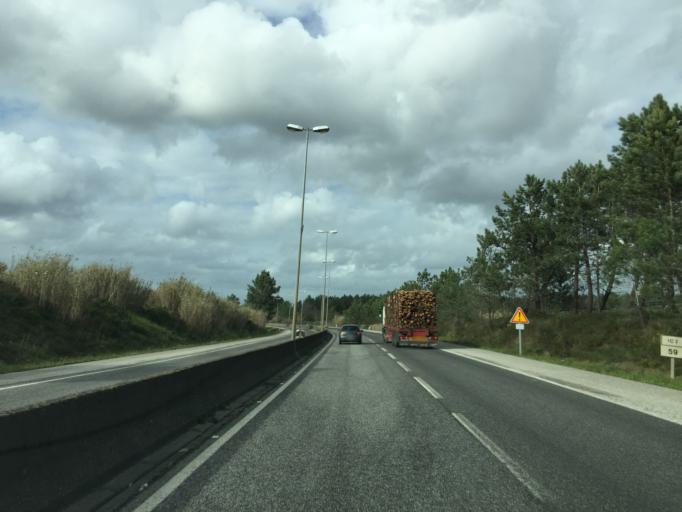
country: PT
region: Lisbon
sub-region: Azambuja
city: Alcoentre
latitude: 39.2292
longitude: -8.9547
